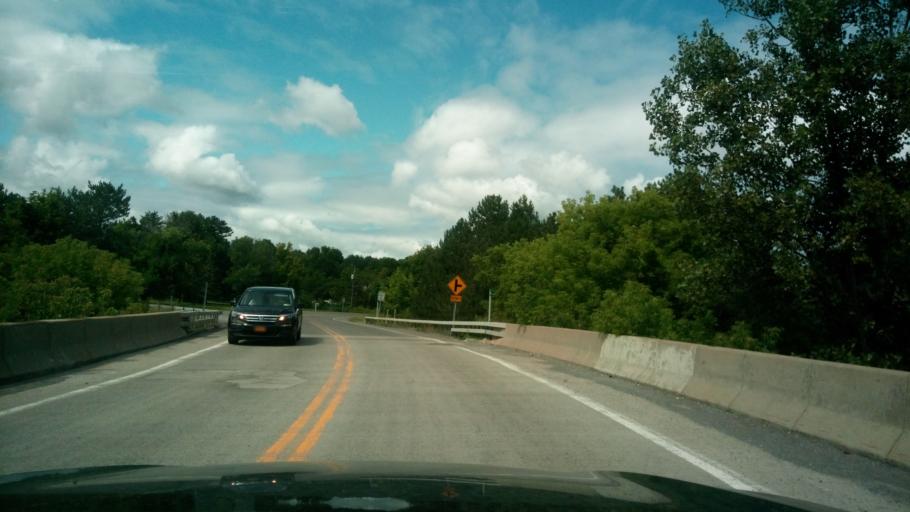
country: US
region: New York
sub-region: Onondaga County
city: East Syracuse
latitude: 43.0039
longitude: -76.0787
